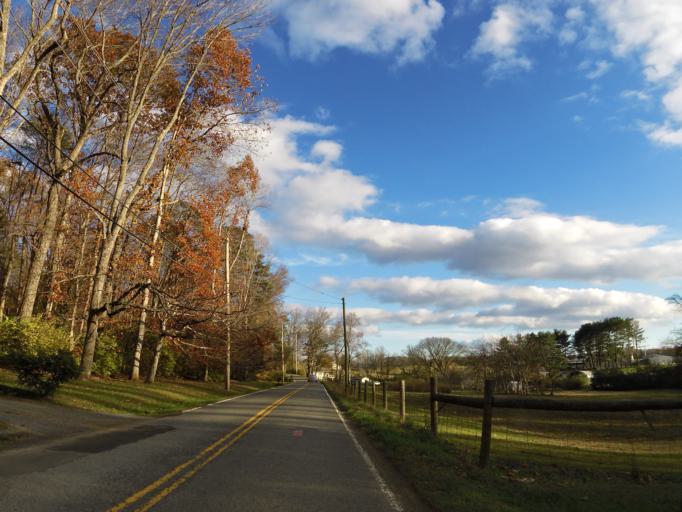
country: US
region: Tennessee
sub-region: Knox County
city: Knoxville
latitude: 35.9045
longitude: -83.9588
